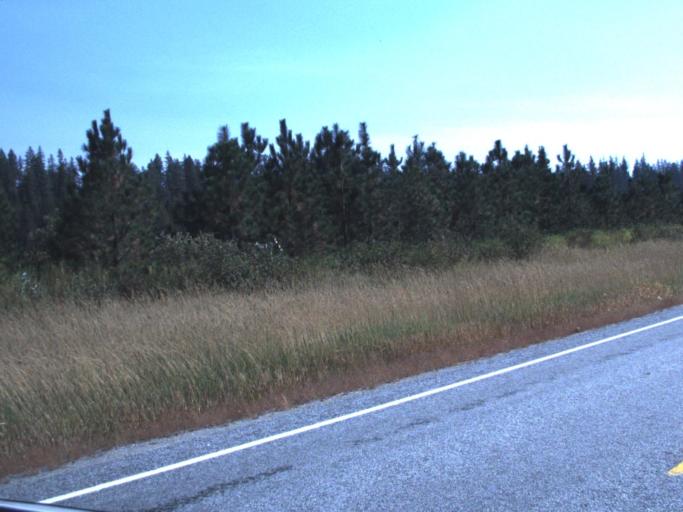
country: US
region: Washington
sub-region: Pend Oreille County
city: Newport
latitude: 48.2886
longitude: -117.2845
